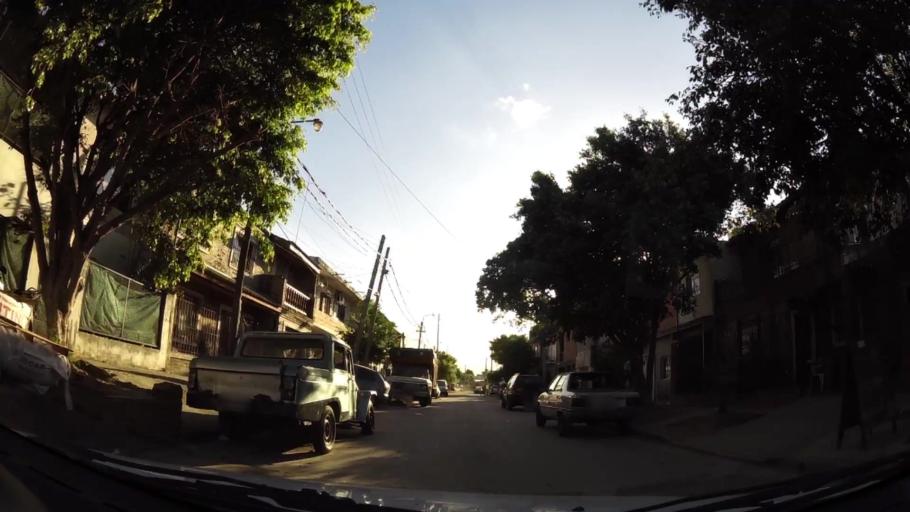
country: AR
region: Buenos Aires
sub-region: Partido de San Isidro
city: San Isidro
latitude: -34.4704
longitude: -58.5427
